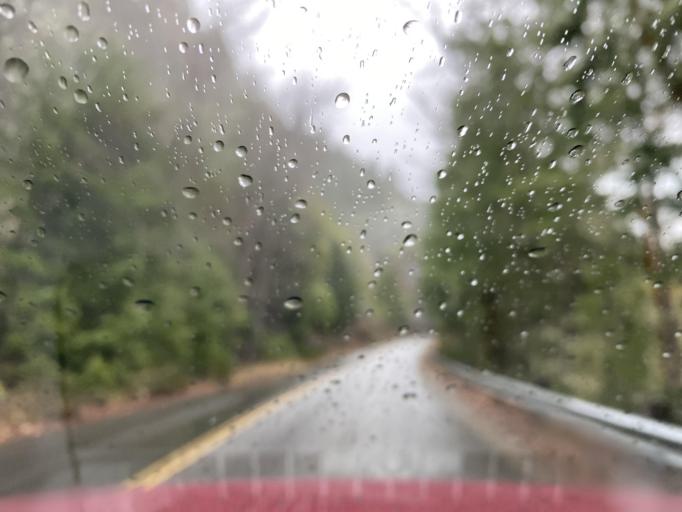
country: US
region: Oregon
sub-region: Lane County
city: Oakridge
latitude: 43.6872
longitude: -122.4410
